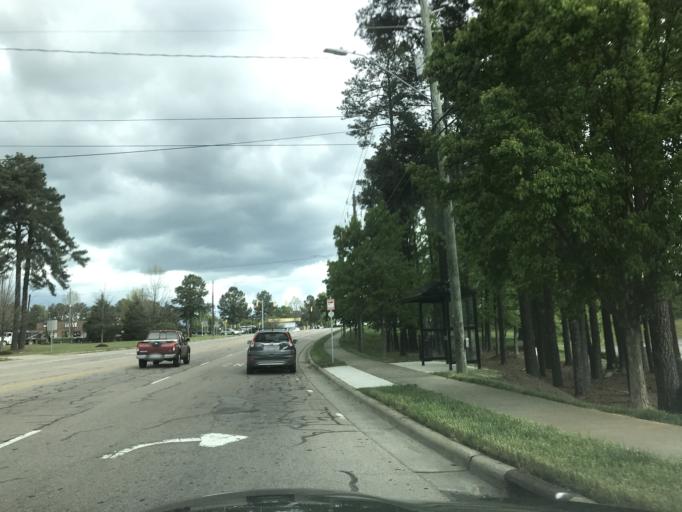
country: US
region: North Carolina
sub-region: Wake County
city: West Raleigh
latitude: 35.7839
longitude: -78.7218
